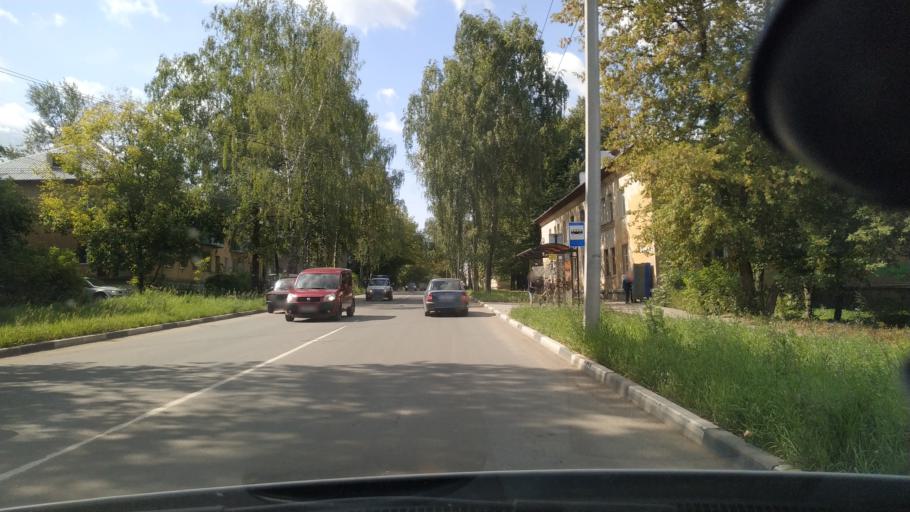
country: RU
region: Rjazan
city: Ryazan'
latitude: 54.6125
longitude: 39.7066
